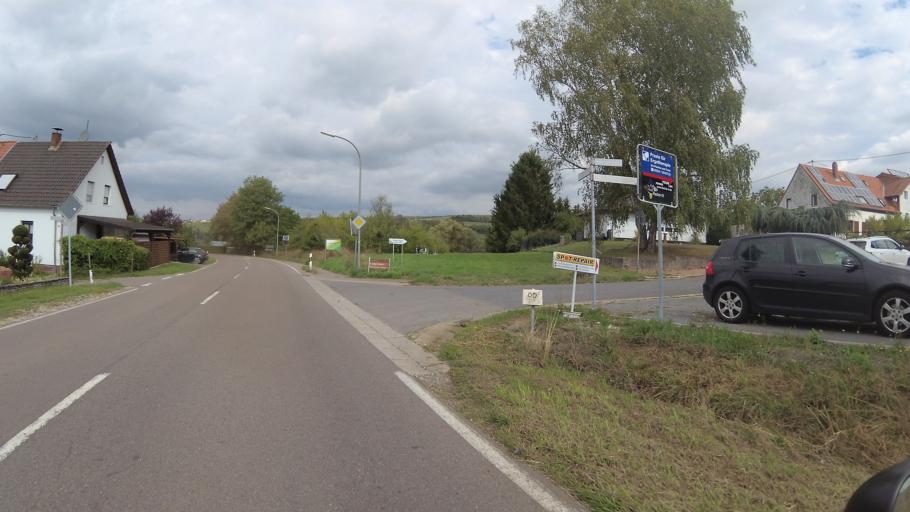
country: FR
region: Lorraine
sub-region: Departement de la Moselle
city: Bliesbruck
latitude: 49.1323
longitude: 7.1394
